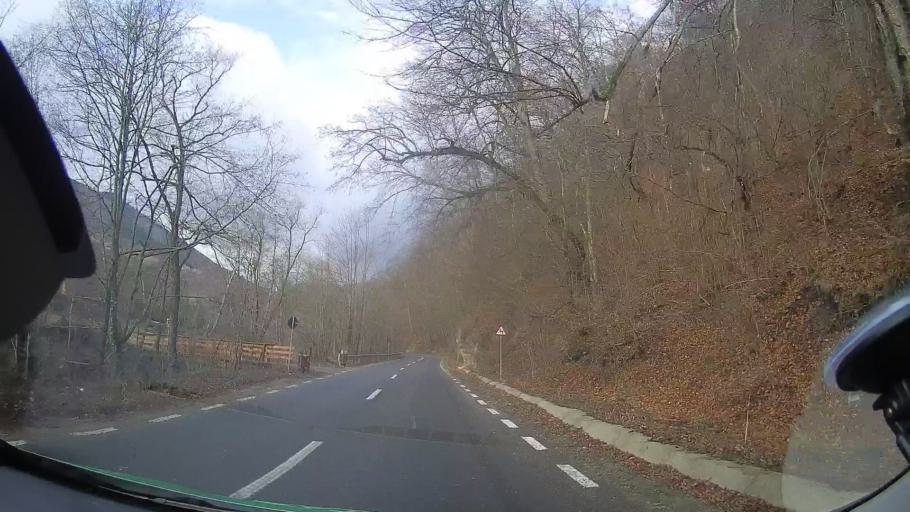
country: RO
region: Cluj
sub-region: Comuna Valea Ierii
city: Valea Ierii
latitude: 46.6380
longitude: 23.3663
